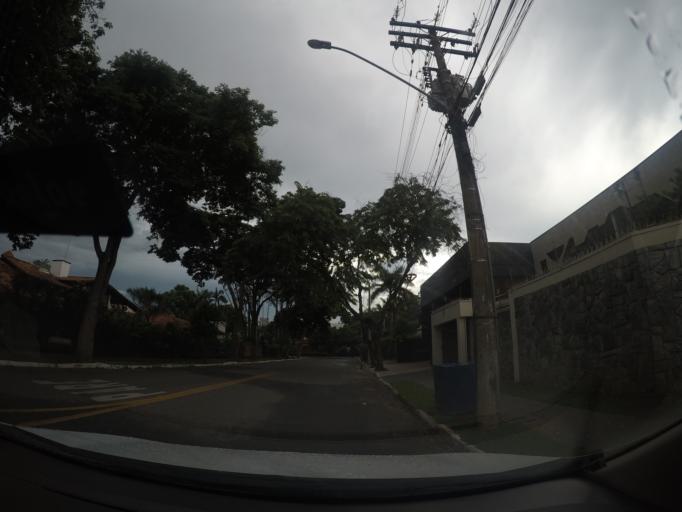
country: BR
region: Goias
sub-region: Goiania
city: Goiania
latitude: -16.7025
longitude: -49.2616
